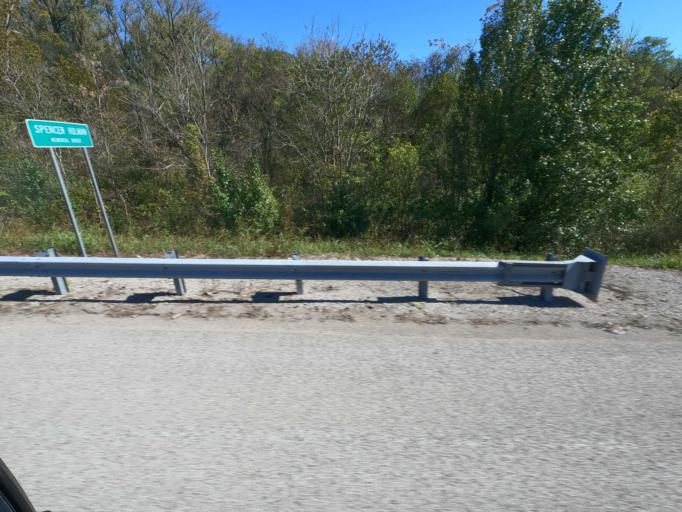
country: US
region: Tennessee
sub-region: Maury County
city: Mount Pleasant
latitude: 35.5024
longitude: -87.2317
